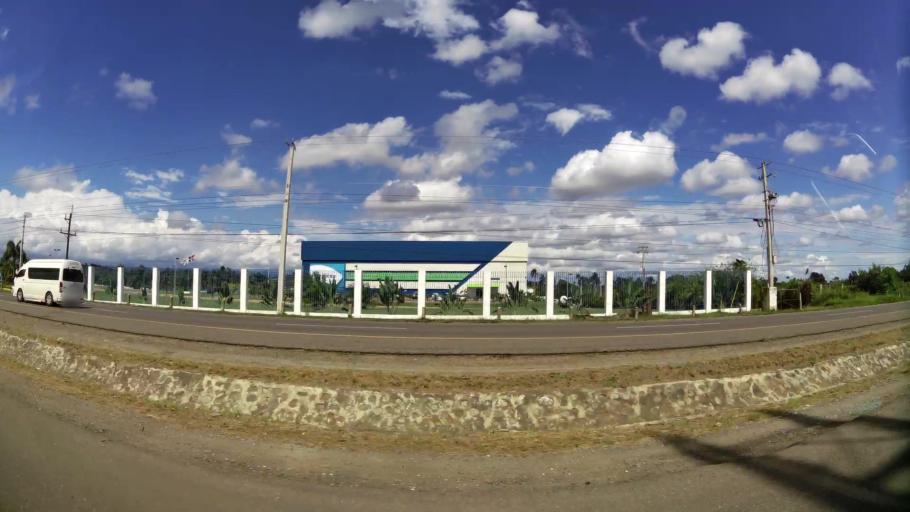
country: DO
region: La Vega
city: Rio Verde Arriba
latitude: 19.3346
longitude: -70.5957
